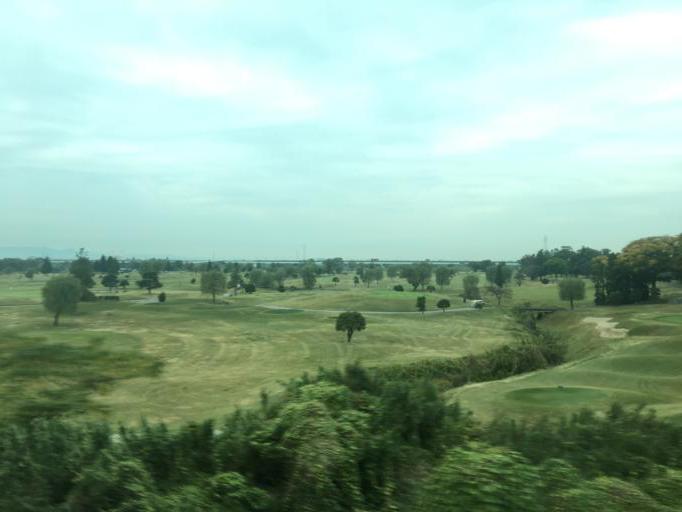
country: JP
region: Saitama
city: Kamifukuoka
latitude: 35.9092
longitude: 139.5525
